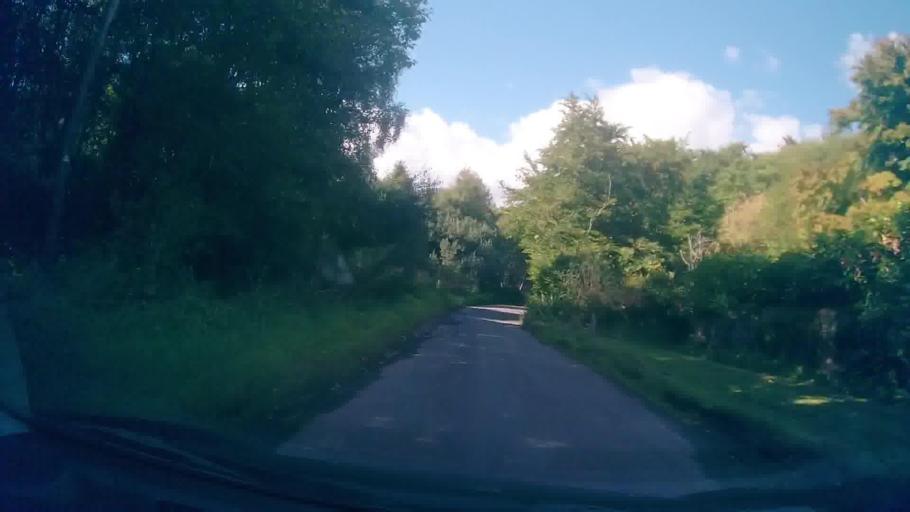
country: GB
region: Wales
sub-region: Merthyr Tydfil County Borough
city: Merthyr Tydfil
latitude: 51.8332
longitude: -3.3823
